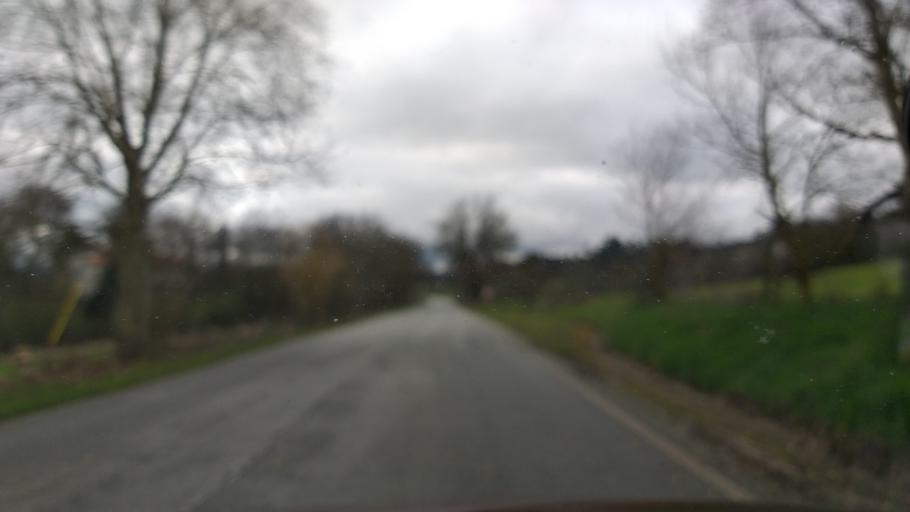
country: PT
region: Guarda
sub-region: Celorico da Beira
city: Celorico da Beira
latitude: 40.6858
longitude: -7.3750
